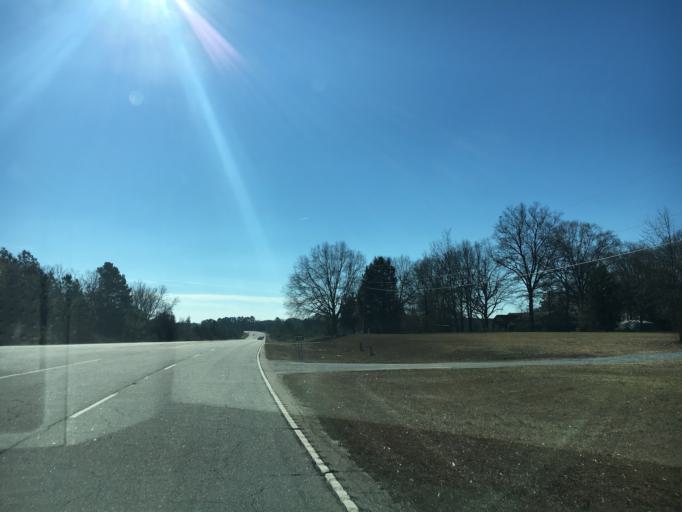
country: US
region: South Carolina
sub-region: Anderson County
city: Homeland Park
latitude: 34.4007
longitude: -82.6881
